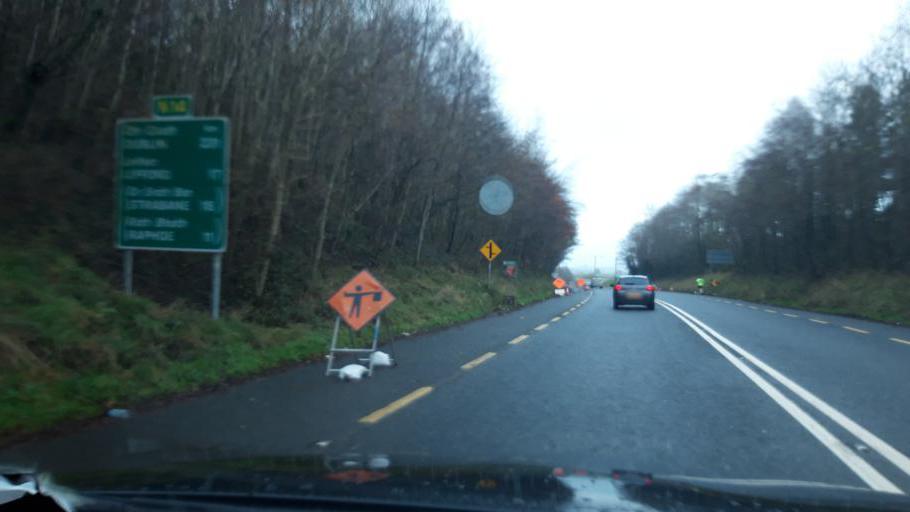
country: IE
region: Ulster
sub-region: County Donegal
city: Raphoe
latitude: 54.9430
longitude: -7.6332
